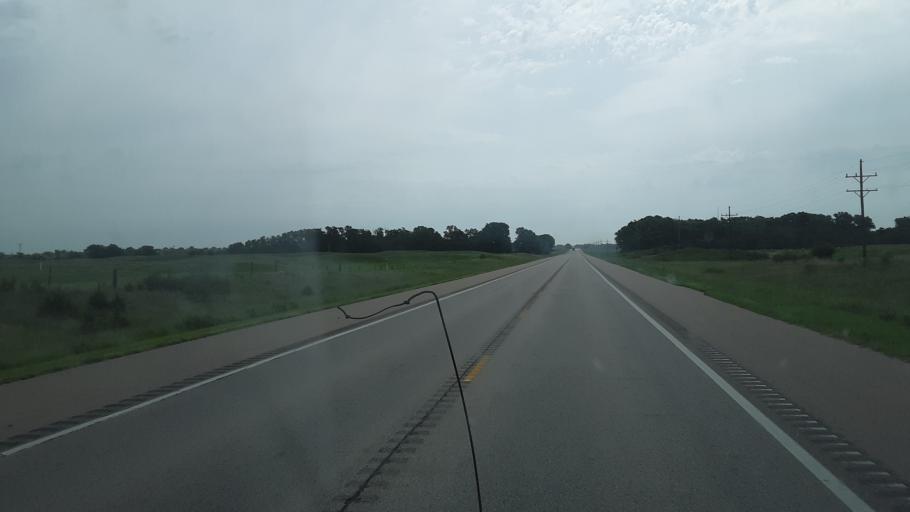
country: US
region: Kansas
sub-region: Stafford County
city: Stafford
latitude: 37.9551
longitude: -98.4592
